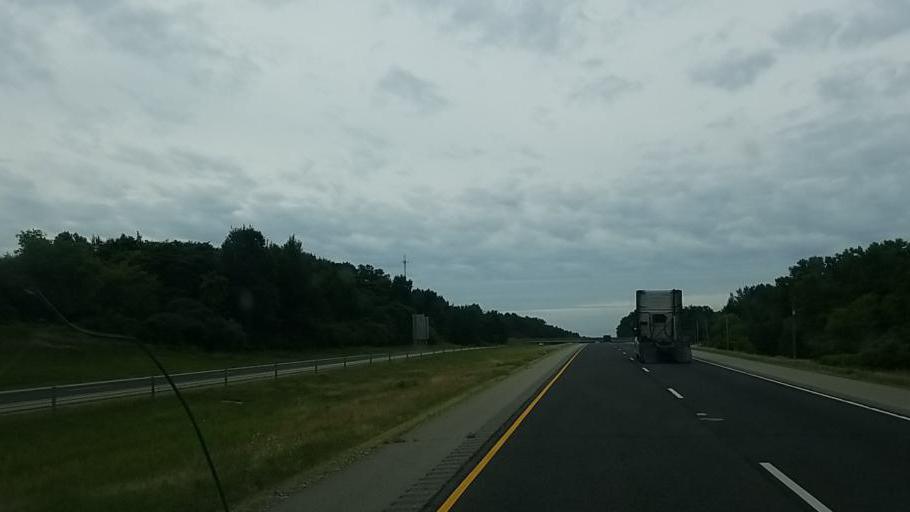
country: US
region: Indiana
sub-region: Steuben County
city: Angola
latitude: 41.6867
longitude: -85.0042
